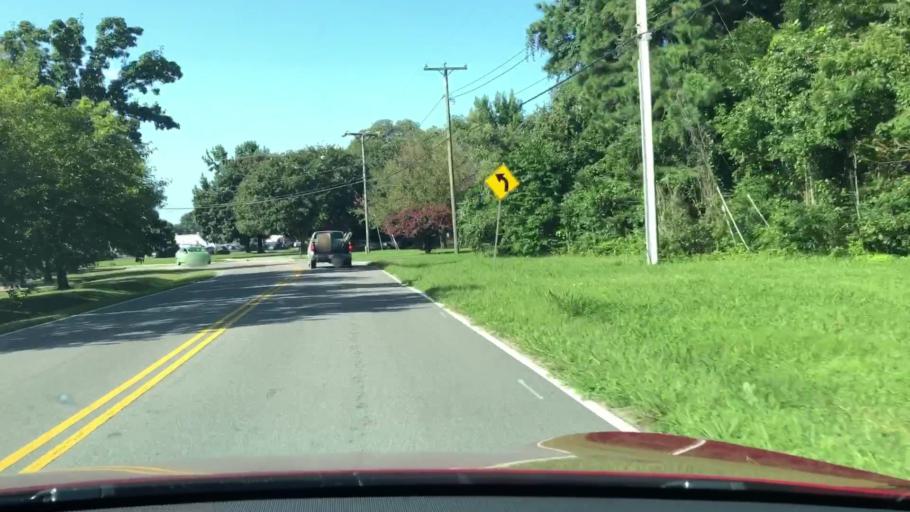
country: US
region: Virginia
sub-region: City of Virginia Beach
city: Virginia Beach
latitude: 36.8455
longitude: -76.0353
